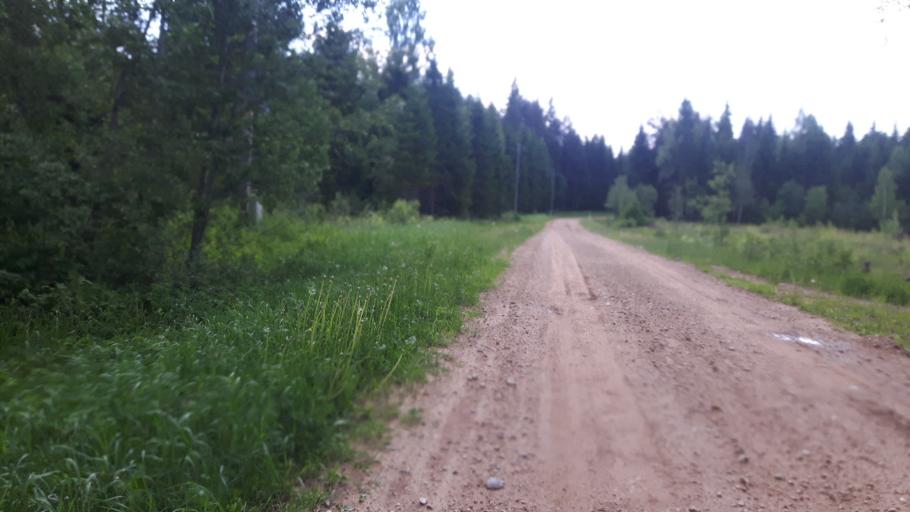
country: EE
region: Paernumaa
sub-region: Vaendra vald (alev)
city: Vandra
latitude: 58.7240
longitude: 25.0362
